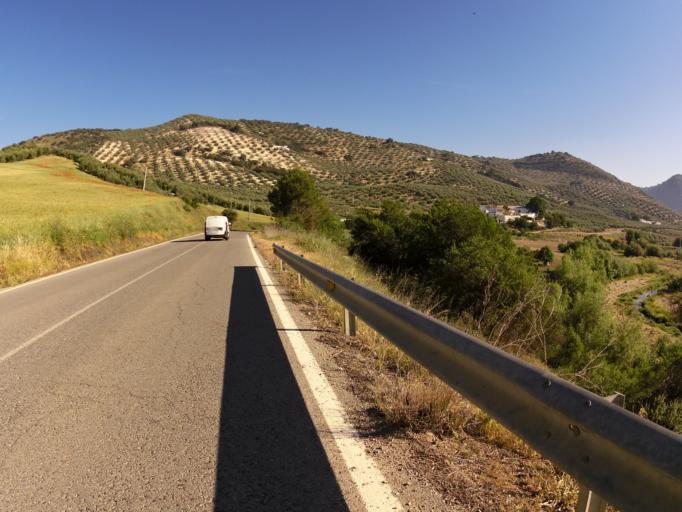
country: ES
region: Andalusia
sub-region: Provincia de Granada
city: Huetor-Tajar
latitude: 37.2583
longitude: -4.0839
